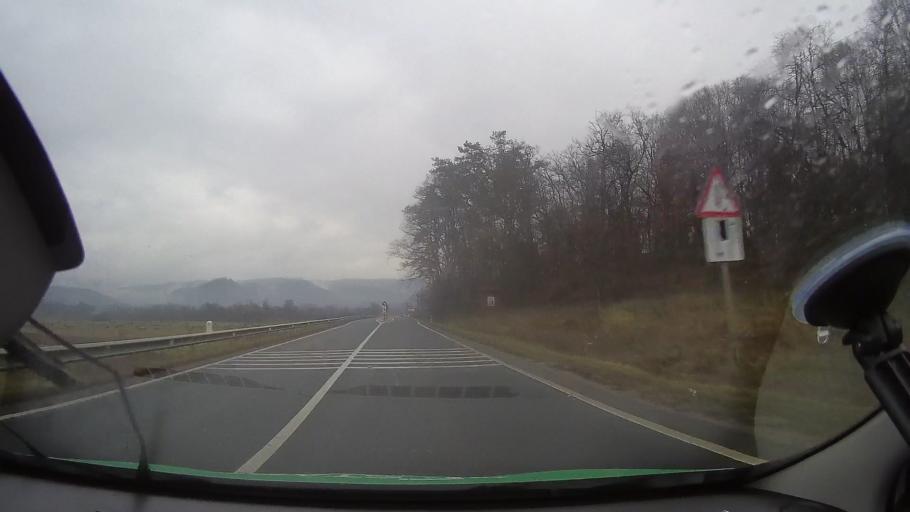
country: RO
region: Hunedoara
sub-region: Comuna Baia de Cris
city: Baia de Cris
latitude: 46.1774
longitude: 22.6983
